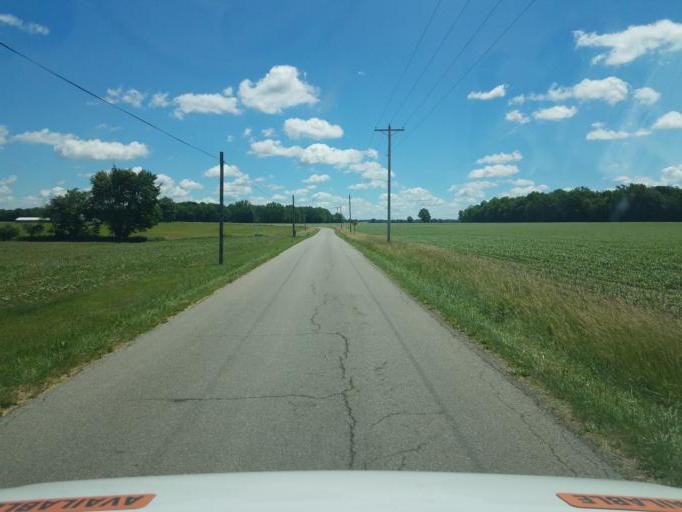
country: US
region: Ohio
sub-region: Crawford County
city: Galion
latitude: 40.7404
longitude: -82.8901
